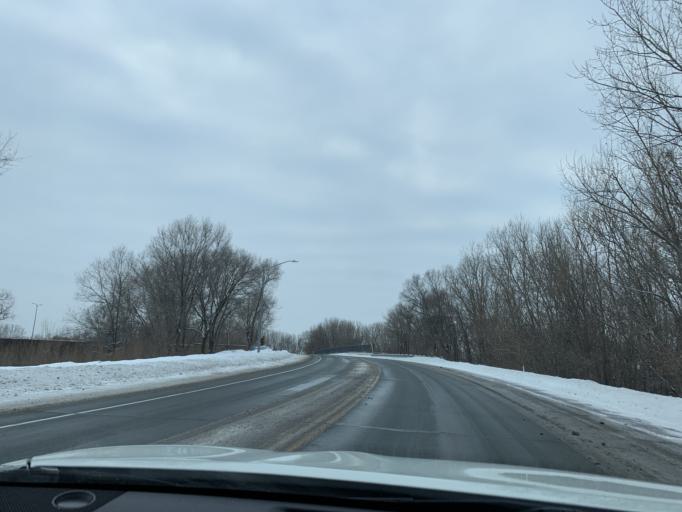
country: US
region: Minnesota
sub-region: Anoka County
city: Coon Rapids
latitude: 45.1638
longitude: -93.2839
